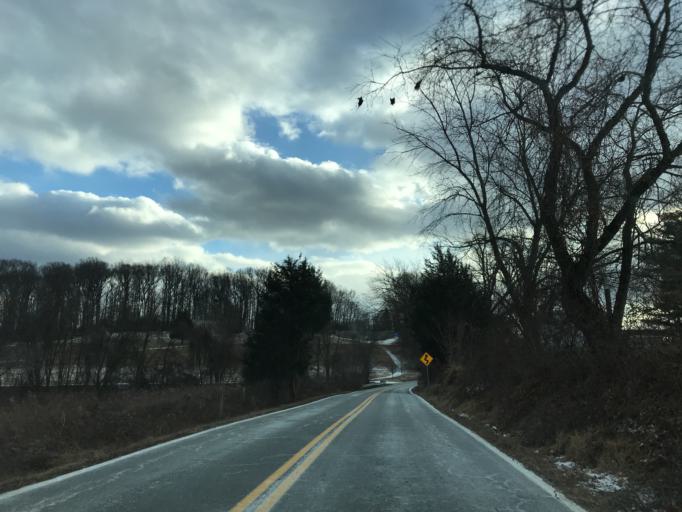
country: US
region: Maryland
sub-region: Harford County
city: Bel Air North
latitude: 39.6211
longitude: -76.3749
